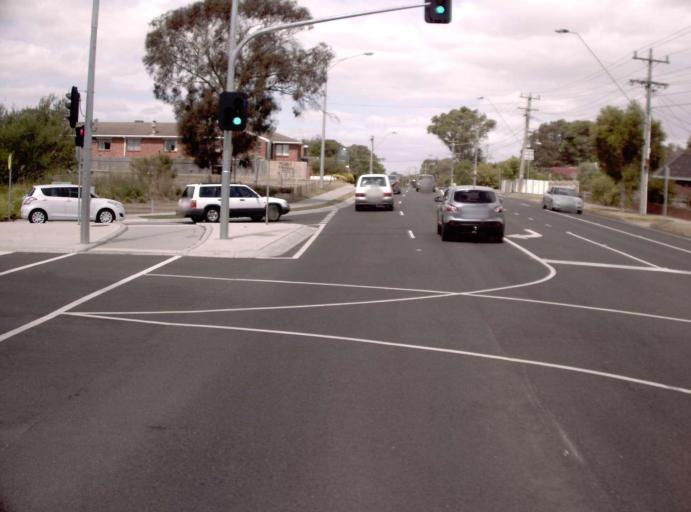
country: AU
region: Victoria
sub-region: Monash
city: Oakleigh South
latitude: -37.9243
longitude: 145.0853
